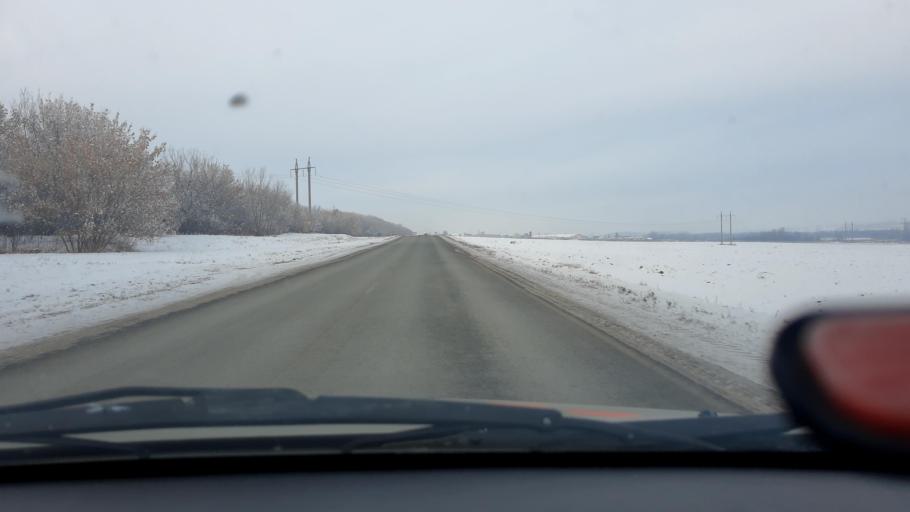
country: RU
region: Bashkortostan
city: Avdon
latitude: 54.4004
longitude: 55.8055
